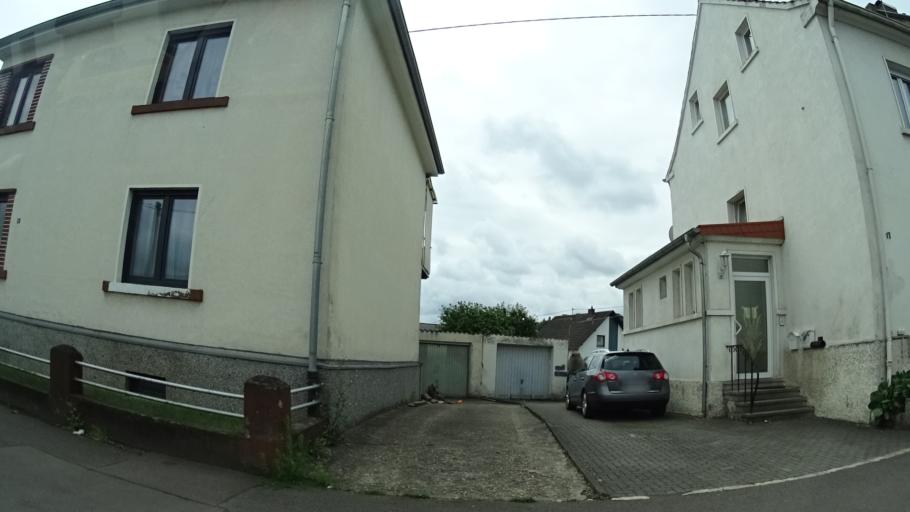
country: DE
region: Saarland
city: Merzig
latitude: 49.4416
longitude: 6.6194
